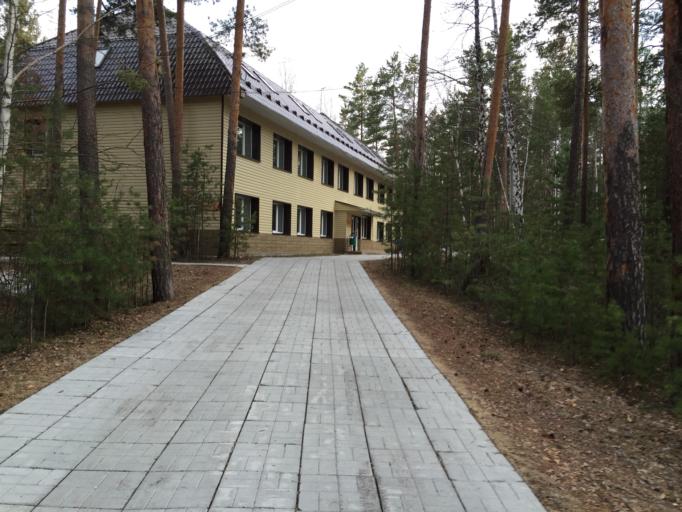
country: RU
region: Chelyabinsk
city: Kyshtym
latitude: 55.6155
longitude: 60.6377
